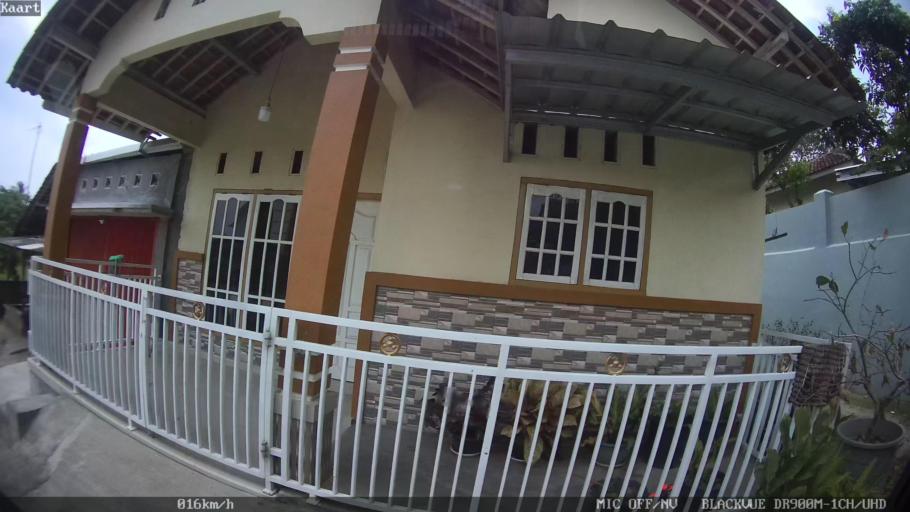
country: ID
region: Lampung
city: Pringsewu
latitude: -5.3469
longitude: 104.9786
